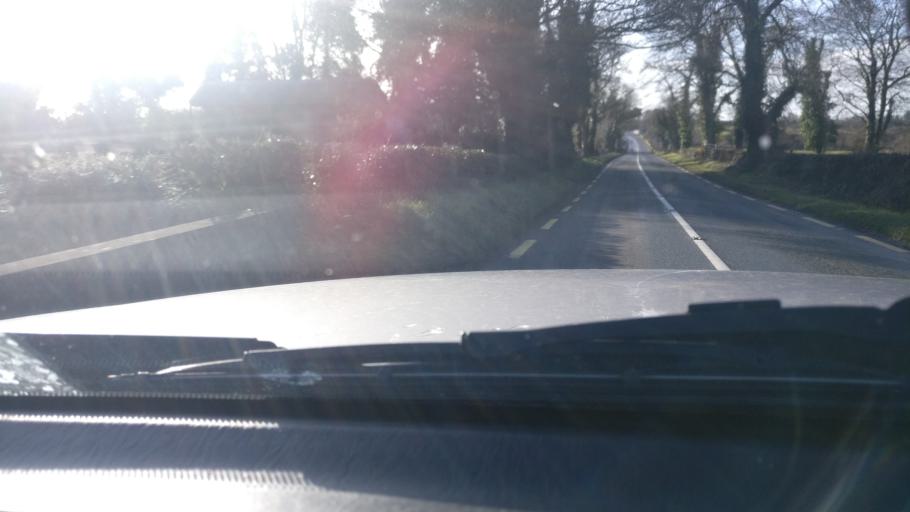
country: IE
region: Leinster
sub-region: An Iarmhi
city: Moate
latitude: 53.5859
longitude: -7.7268
